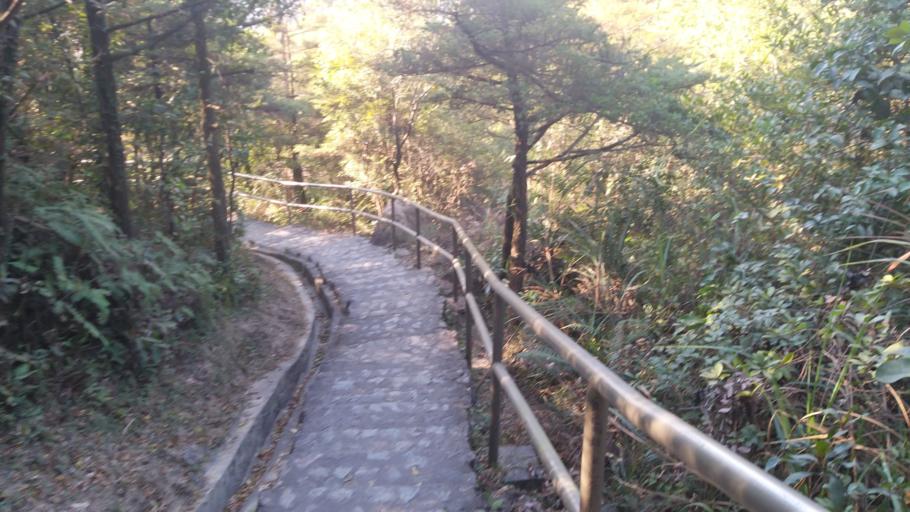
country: HK
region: Tuen Mun
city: Tuen Mun
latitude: 22.3999
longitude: 113.9856
